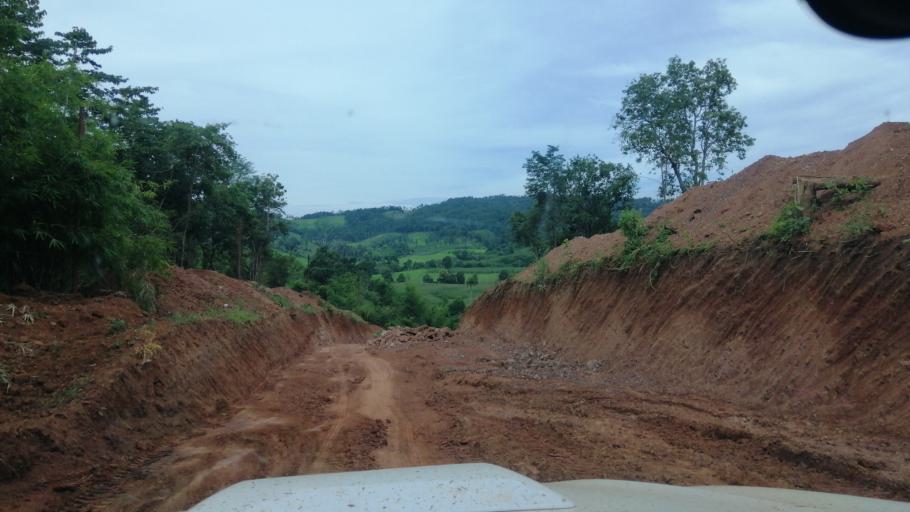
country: TH
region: Loei
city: Na Haeo
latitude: 17.5824
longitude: 101.1454
